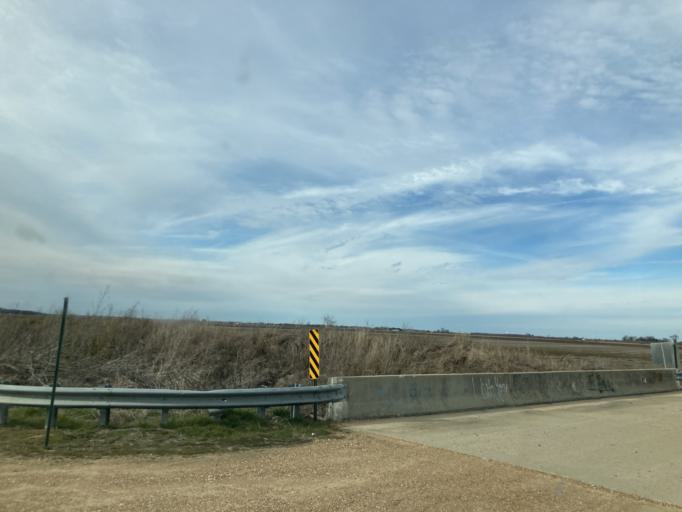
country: US
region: Mississippi
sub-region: Humphreys County
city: Belzoni
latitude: 33.1675
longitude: -90.5553
